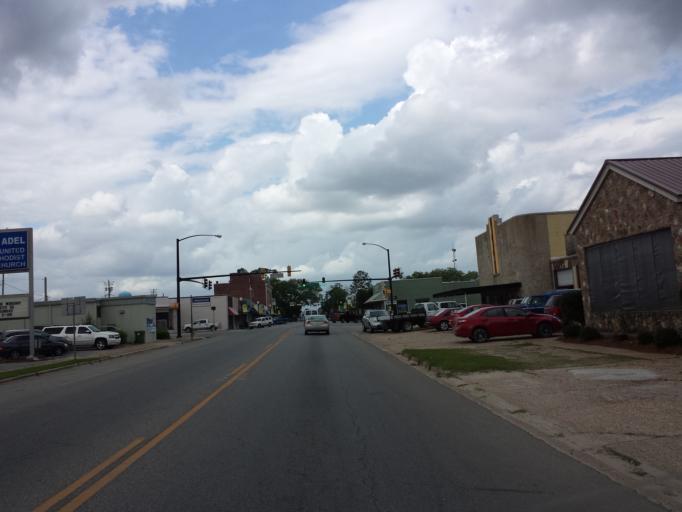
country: US
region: Georgia
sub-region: Cook County
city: Adel
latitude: 31.1351
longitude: -83.4227
